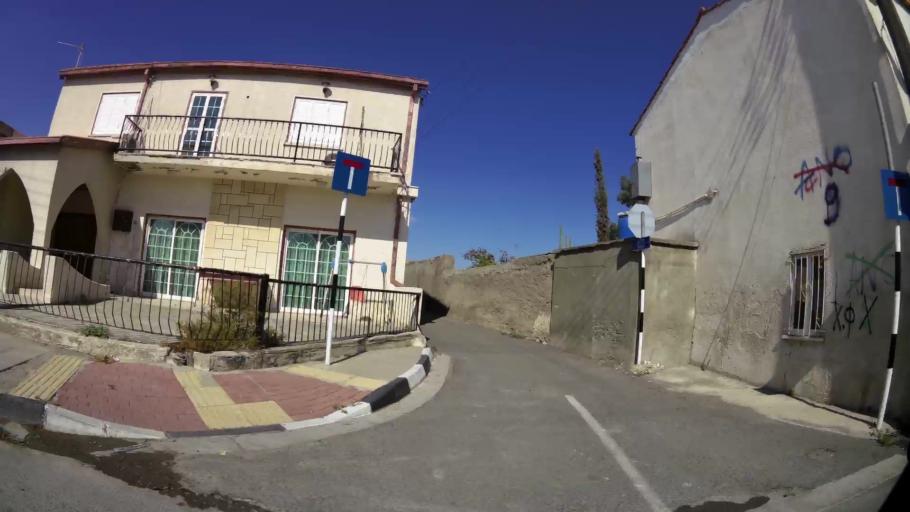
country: CY
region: Larnaka
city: Livadia
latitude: 34.9486
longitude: 33.6325
